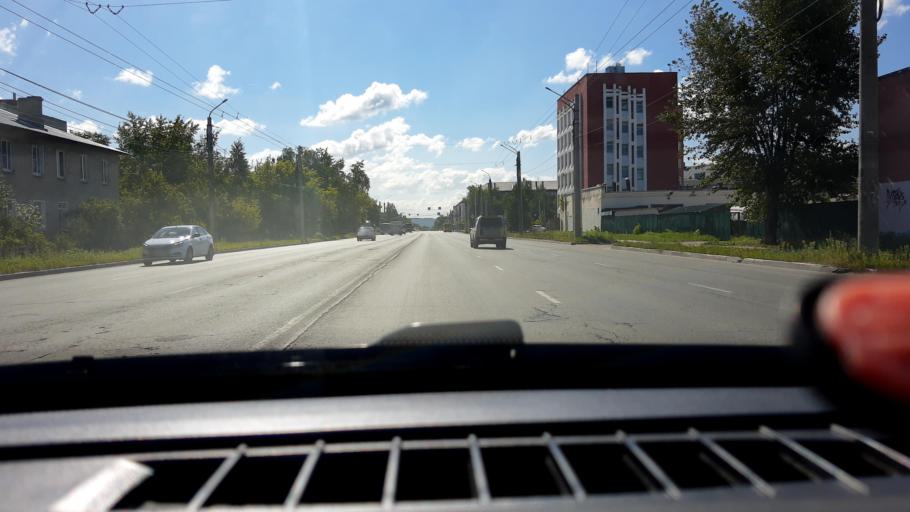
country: RU
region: Nizjnij Novgorod
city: Dzerzhinsk
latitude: 56.2468
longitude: 43.4756
